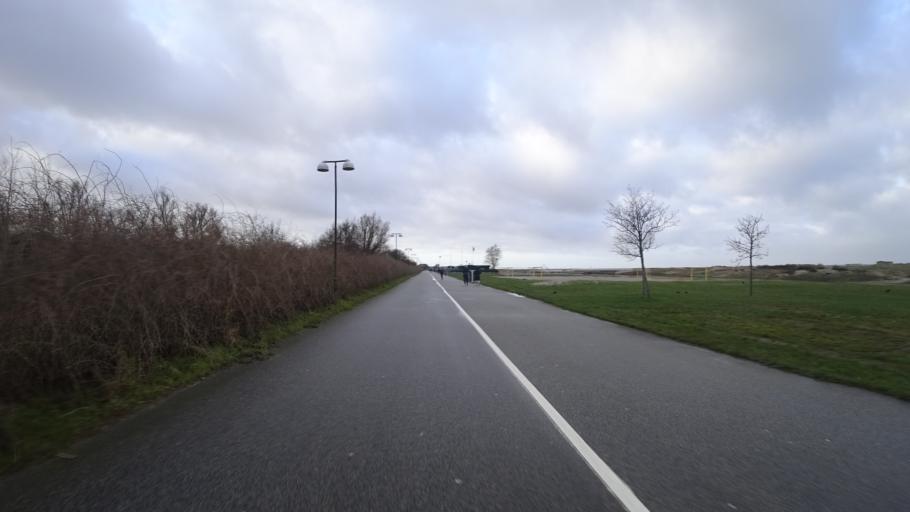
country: SE
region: Skane
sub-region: Malmo
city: Malmoe
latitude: 55.6009
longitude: 12.9623
